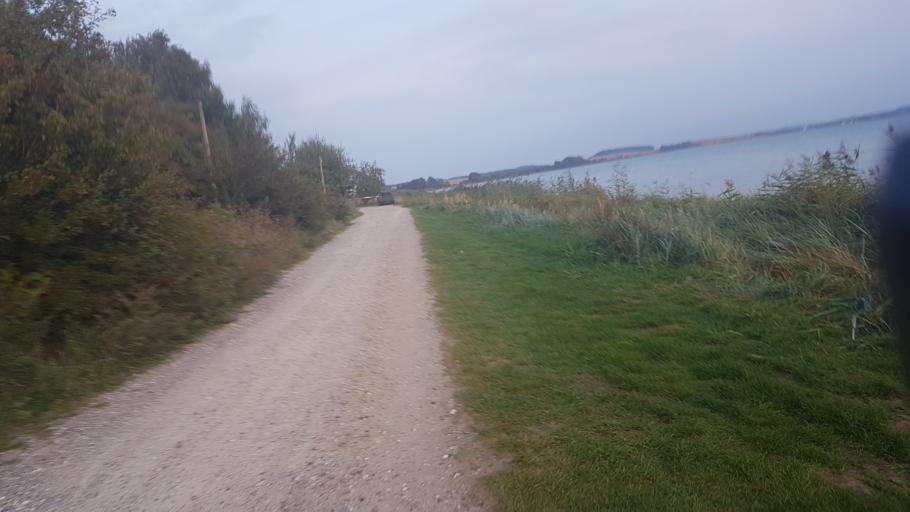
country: DE
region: Mecklenburg-Vorpommern
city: Ostseebad Binz
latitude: 54.3530
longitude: 13.5790
